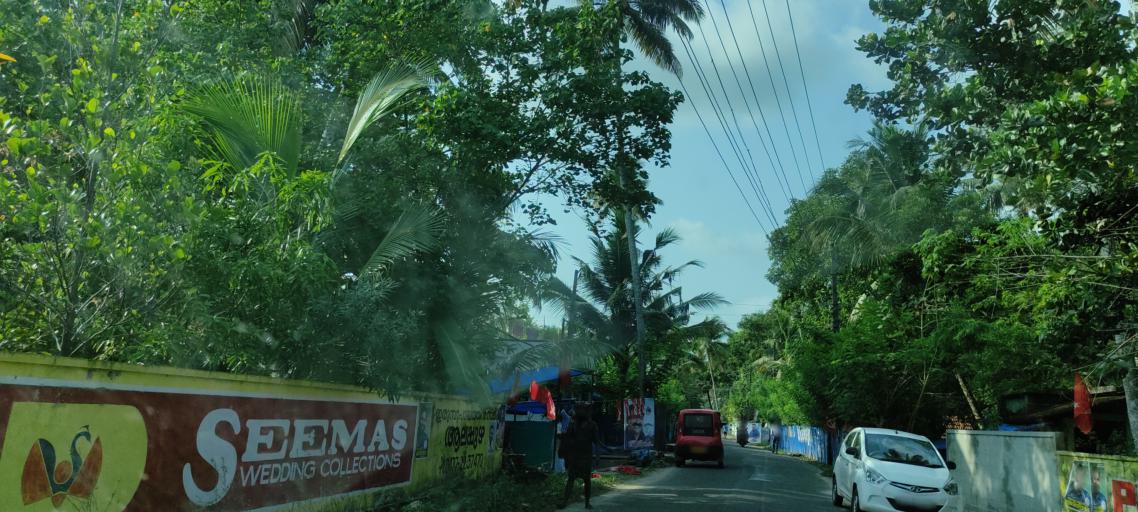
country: IN
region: Kerala
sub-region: Alappuzha
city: Vayalar
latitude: 9.7077
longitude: 76.2889
